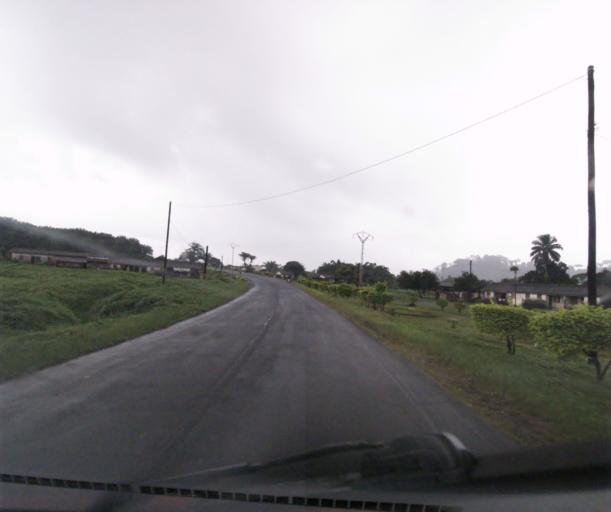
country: CM
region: South-West Province
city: Idenao
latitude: 4.1108
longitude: 8.9886
